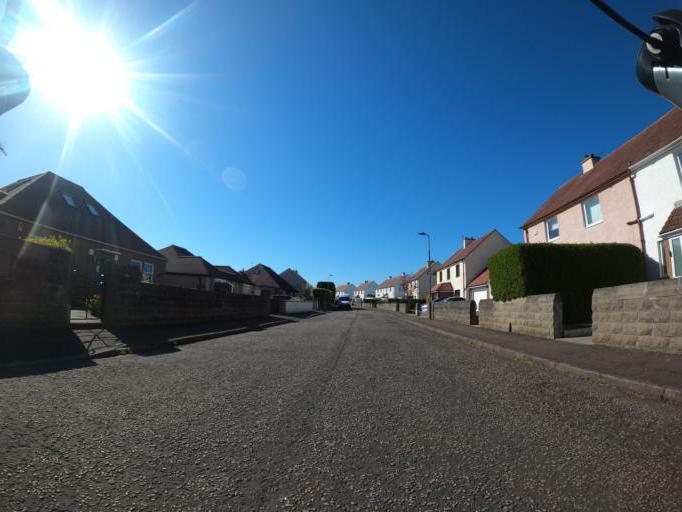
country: GB
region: Scotland
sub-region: Edinburgh
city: Currie
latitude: 55.9431
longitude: -3.3026
